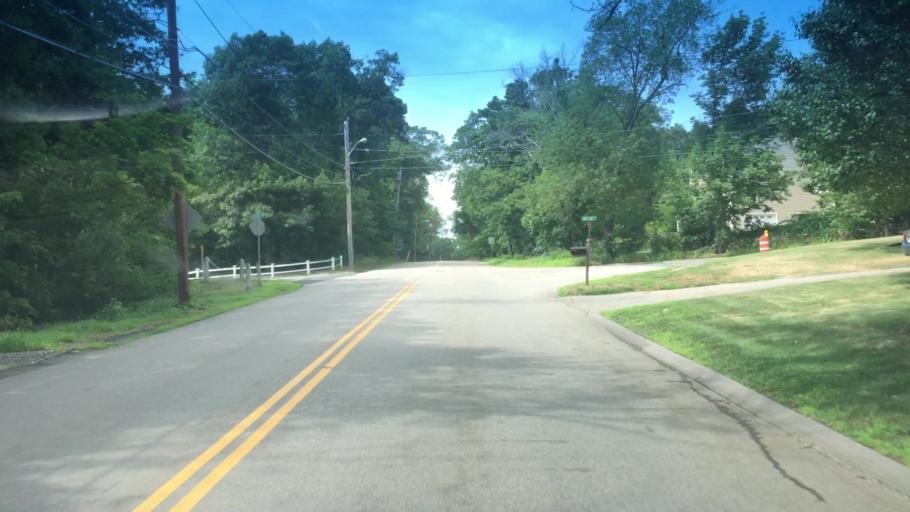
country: US
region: Massachusetts
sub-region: Norfolk County
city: Medway
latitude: 42.1265
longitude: -71.3989
